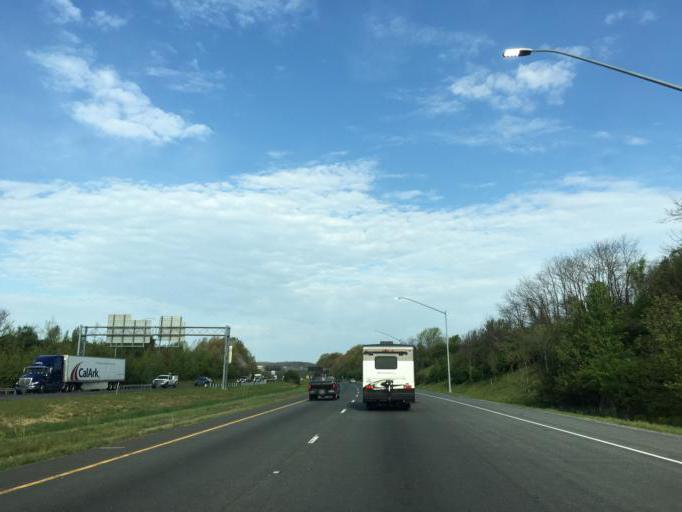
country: US
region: Maryland
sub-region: Frederick County
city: Ballenger Creek
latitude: 39.4023
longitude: -77.4476
